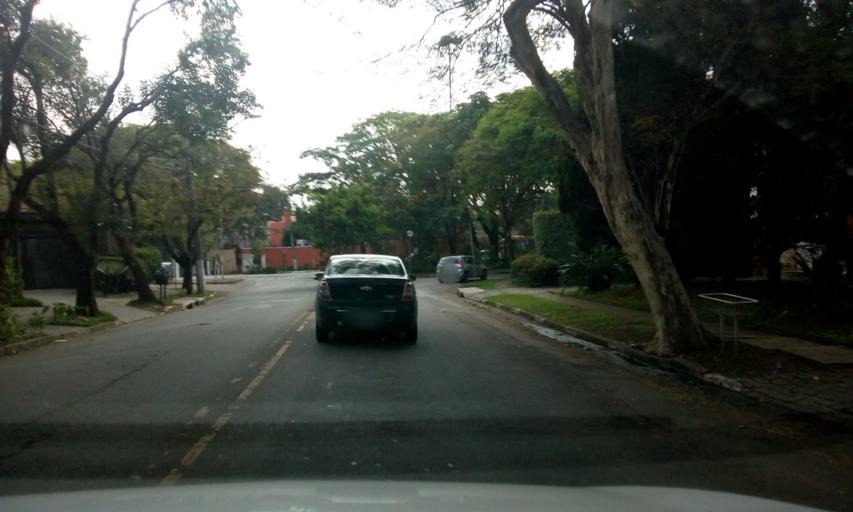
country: BR
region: Sao Paulo
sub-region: Sao Paulo
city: Sao Paulo
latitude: -23.5459
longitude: -46.7129
